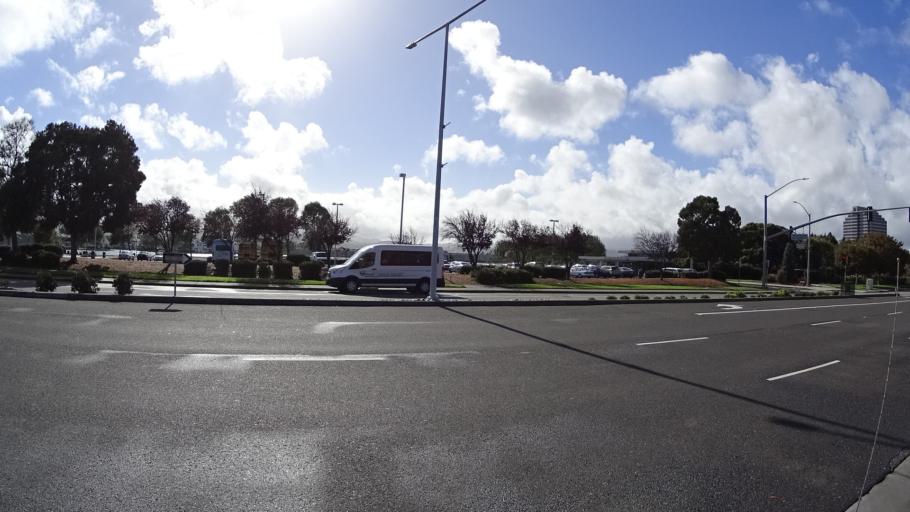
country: US
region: California
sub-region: San Mateo County
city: Foster City
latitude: 37.5572
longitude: -122.2684
